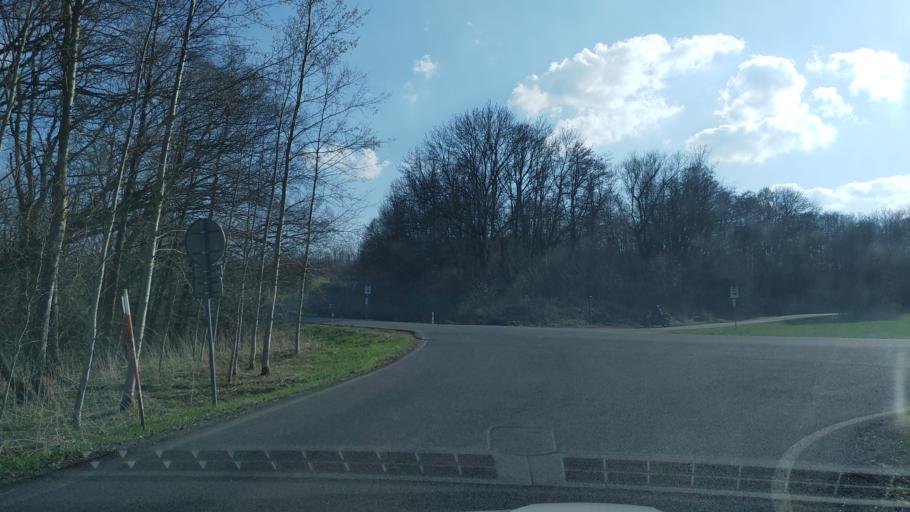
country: CZ
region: Ustecky
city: Vernerice
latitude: 50.6817
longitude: 14.3108
